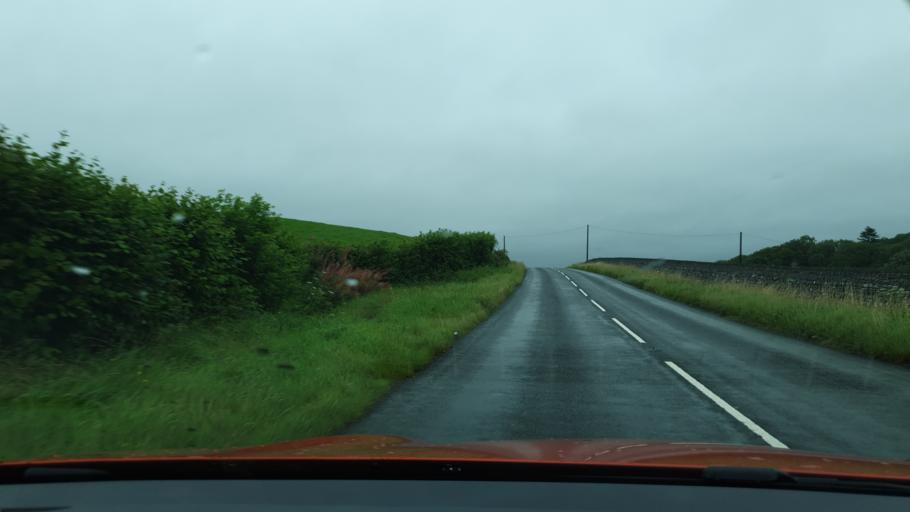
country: GB
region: England
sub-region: Cumbria
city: Ulverston
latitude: 54.2631
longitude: -3.0815
